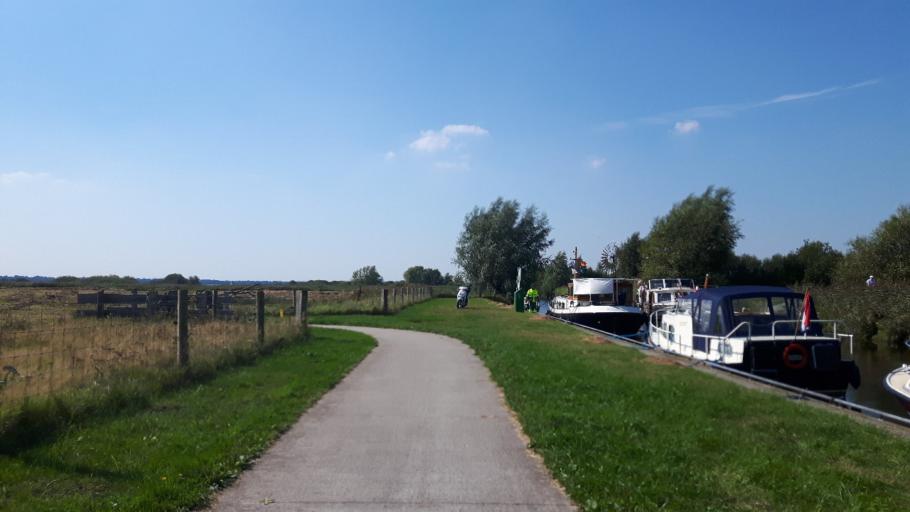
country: NL
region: Groningen
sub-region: Gemeente Hoogezand-Sappemeer
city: Hoogezand
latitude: 53.1318
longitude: 6.7213
